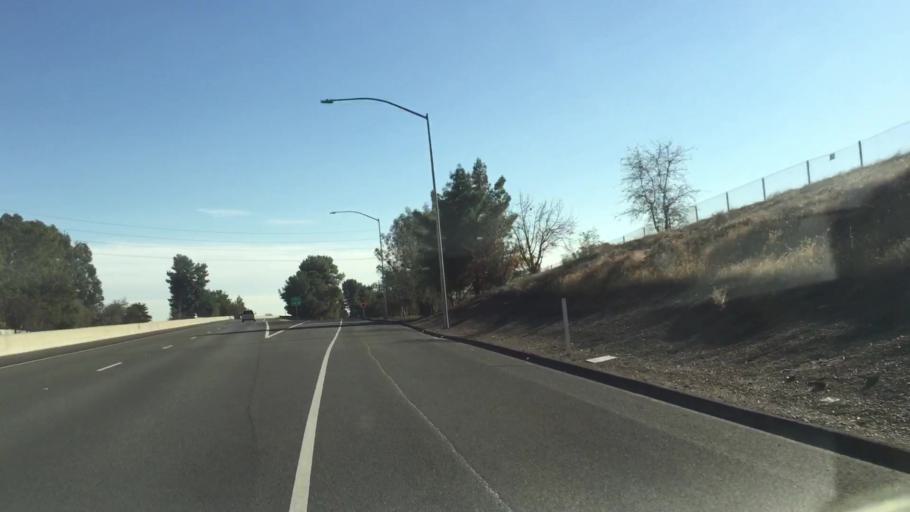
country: US
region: California
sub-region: Butte County
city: Thermalito
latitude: 39.5271
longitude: -121.5758
